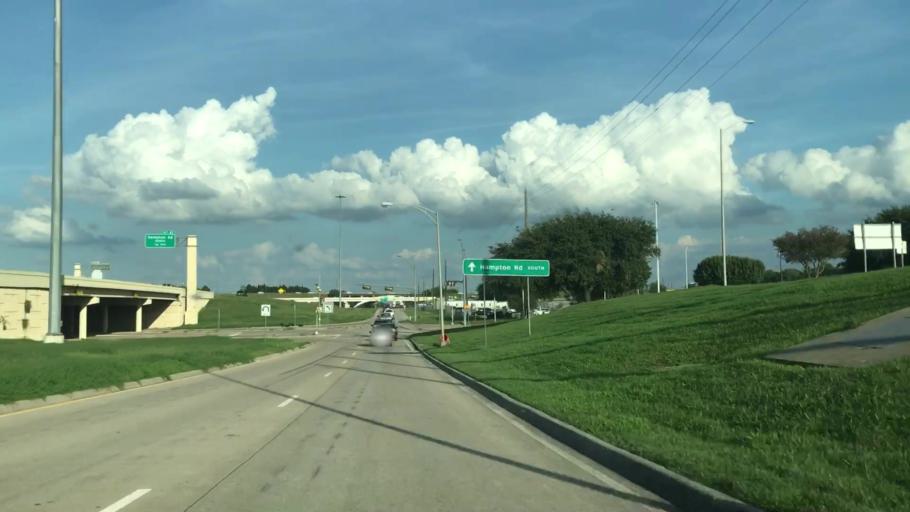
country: US
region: Texas
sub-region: Dallas County
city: Cockrell Hill
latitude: 32.7666
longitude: -96.8637
